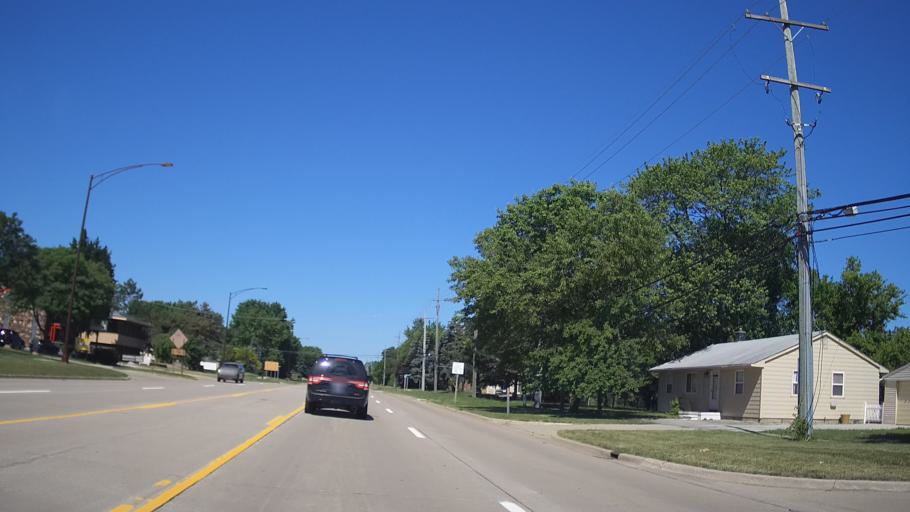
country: US
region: Michigan
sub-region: Oakland County
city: Troy
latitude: 42.5930
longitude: -83.0921
